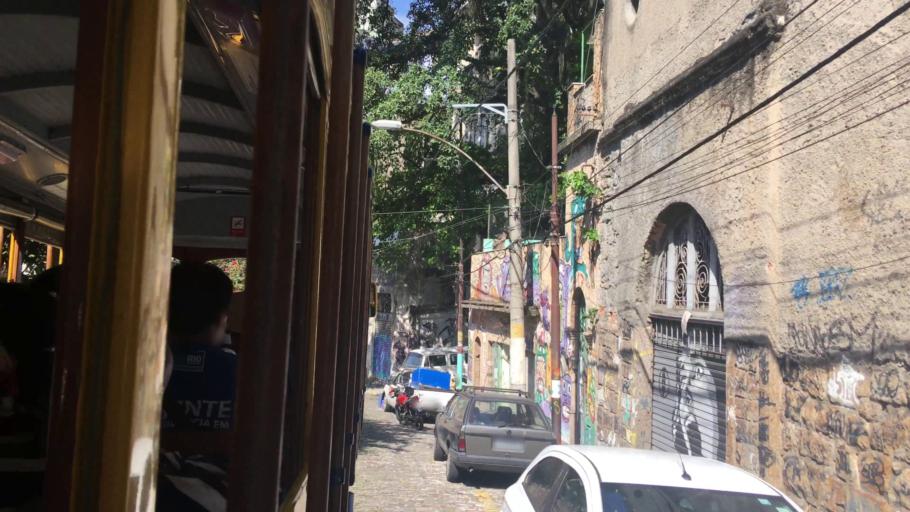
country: BR
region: Rio de Janeiro
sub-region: Rio De Janeiro
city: Rio de Janeiro
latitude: -22.9167
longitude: -43.1815
